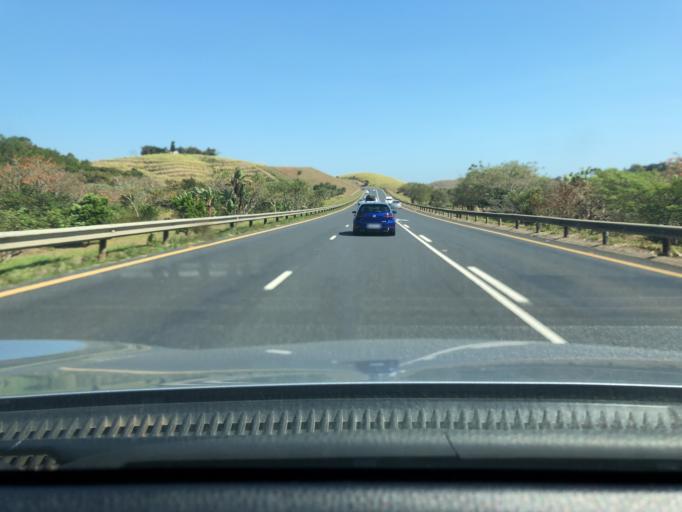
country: ZA
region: KwaZulu-Natal
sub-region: Ugu District Municipality
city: Port Shepstone
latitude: -30.6313
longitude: 30.5212
